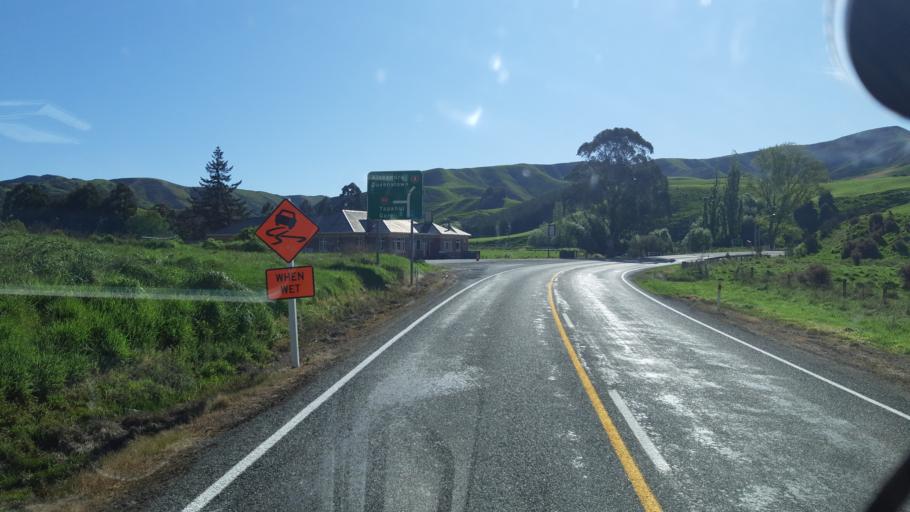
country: NZ
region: Otago
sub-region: Clutha District
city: Balclutha
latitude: -45.7867
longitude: 169.4707
